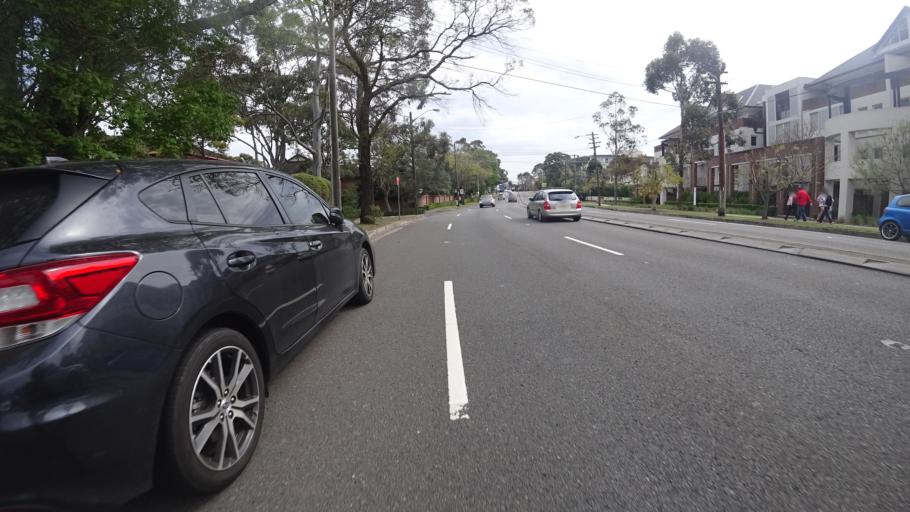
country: AU
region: New South Wales
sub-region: Ku-ring-gai
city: Killara
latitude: -33.7624
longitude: 151.1550
